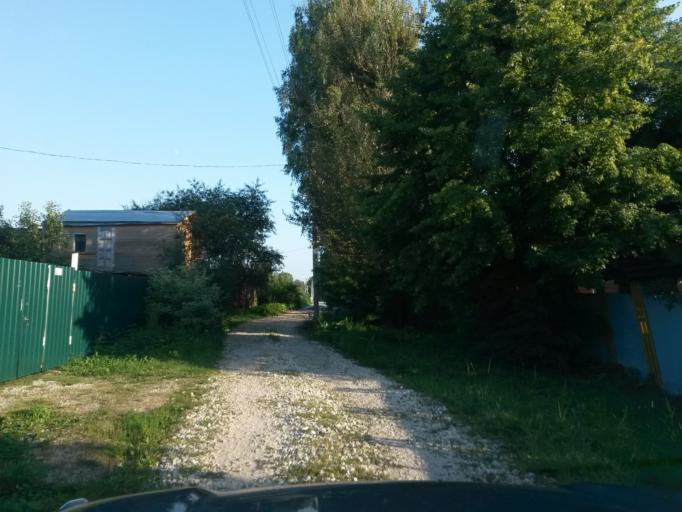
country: RU
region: Moskovskaya
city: Lyubuchany
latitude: 55.2538
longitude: 37.6074
